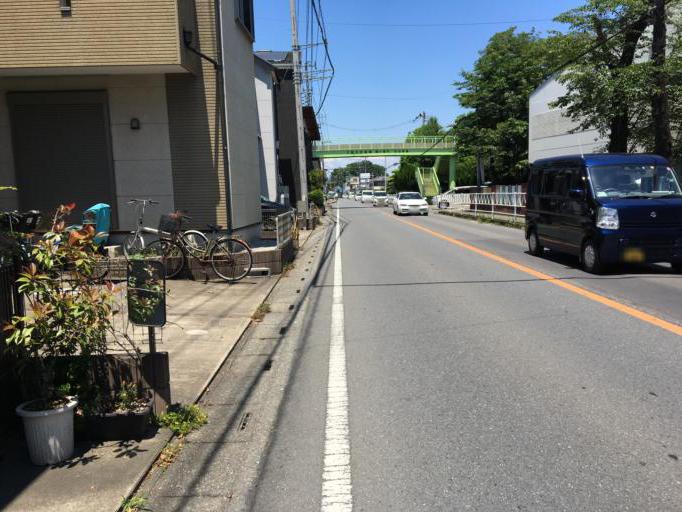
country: JP
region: Saitama
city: Sakado
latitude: 35.9377
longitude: 139.3883
